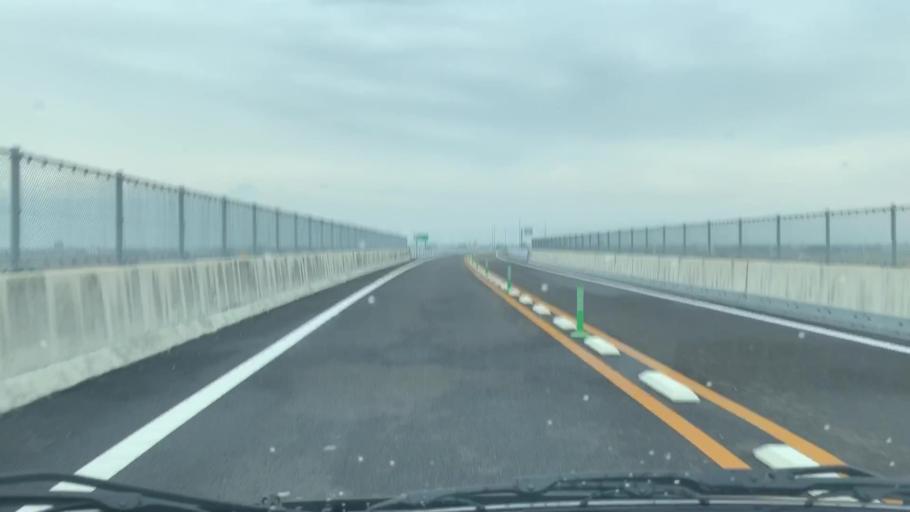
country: JP
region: Saga Prefecture
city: Saga-shi
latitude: 33.2206
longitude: 130.2148
